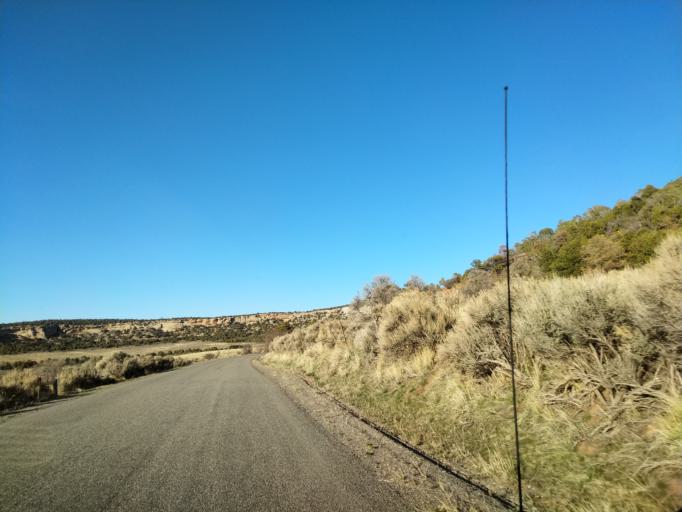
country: US
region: Colorado
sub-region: Mesa County
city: Loma
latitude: 38.9595
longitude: -109.0117
